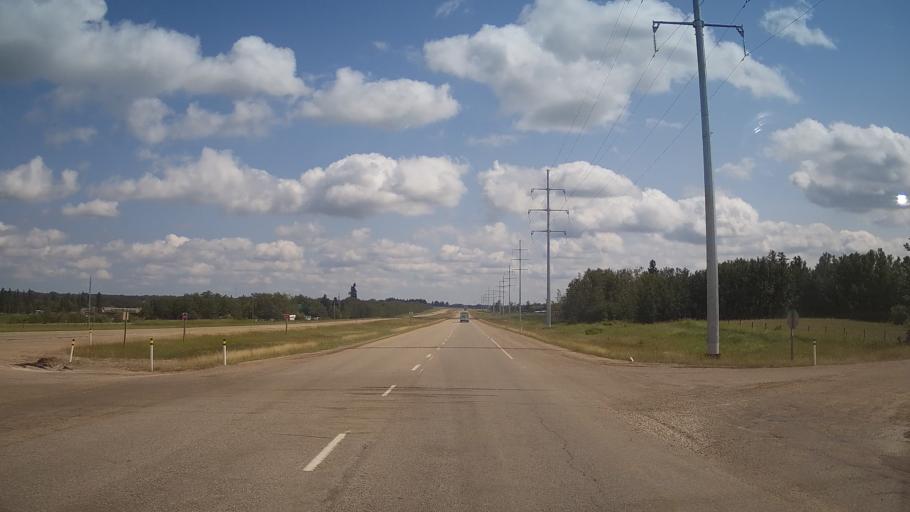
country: CA
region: Alberta
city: Sherwood Park
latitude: 53.4420
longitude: -113.2219
